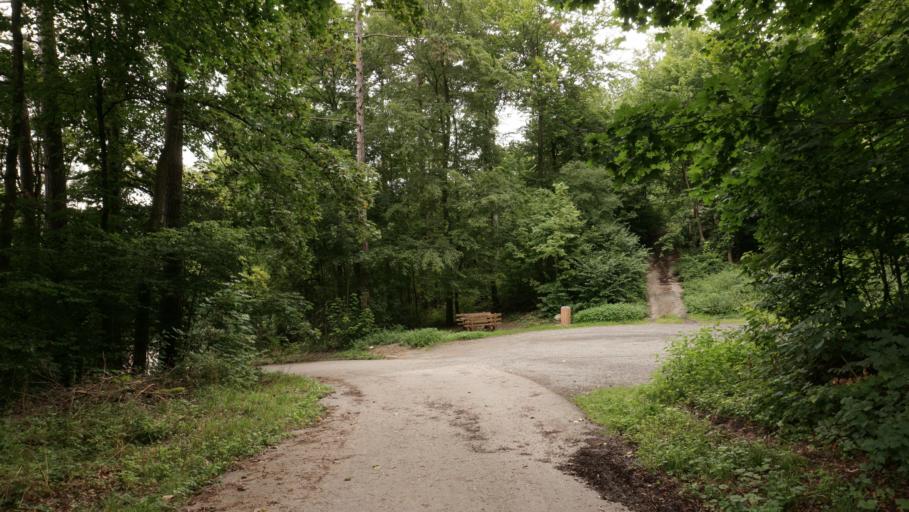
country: DE
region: Baden-Wuerttemberg
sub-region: Karlsruhe Region
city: Neckarzimmern
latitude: 49.3362
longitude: 9.1253
